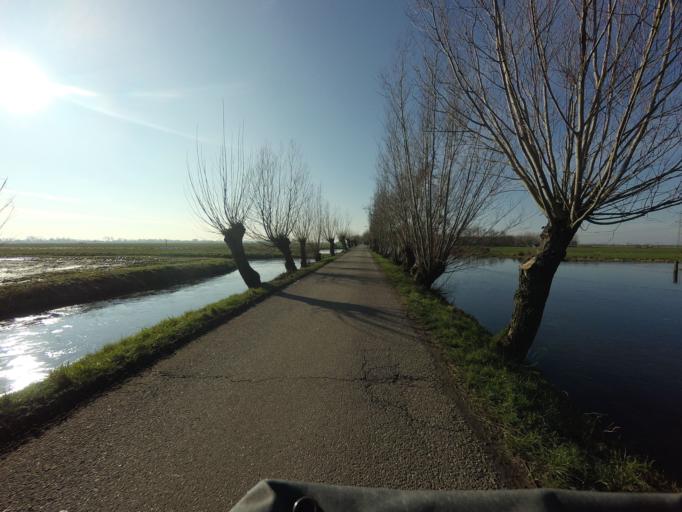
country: NL
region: Utrecht
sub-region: Gemeente Oudewater
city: Oudewater
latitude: 52.0311
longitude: 4.8387
